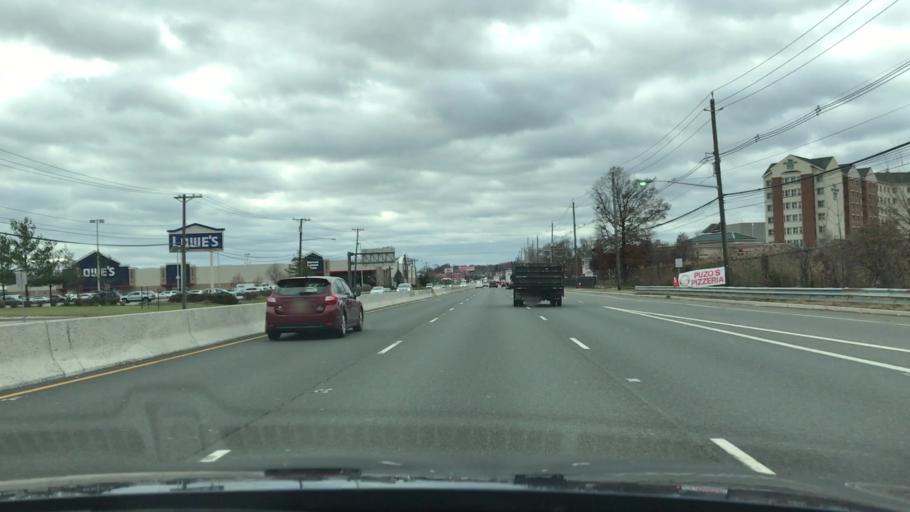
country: US
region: New Jersey
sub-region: Bergen County
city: East Rutherford
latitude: 40.8307
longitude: -74.0910
